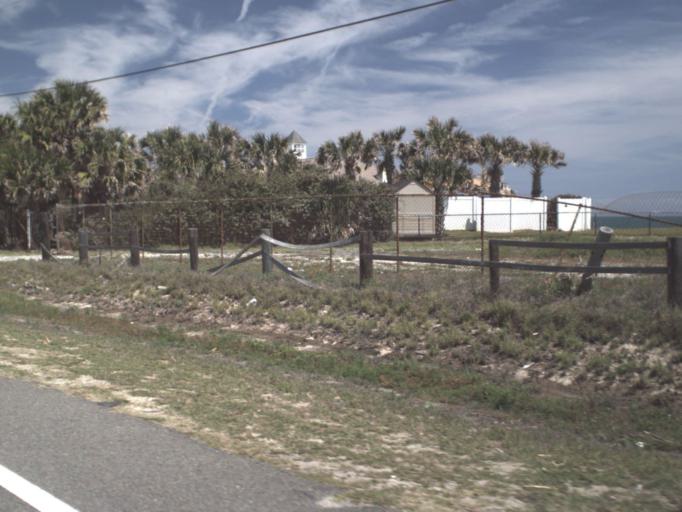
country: US
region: Florida
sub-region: Flagler County
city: Flagler Beach
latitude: 29.5244
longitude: -81.1493
